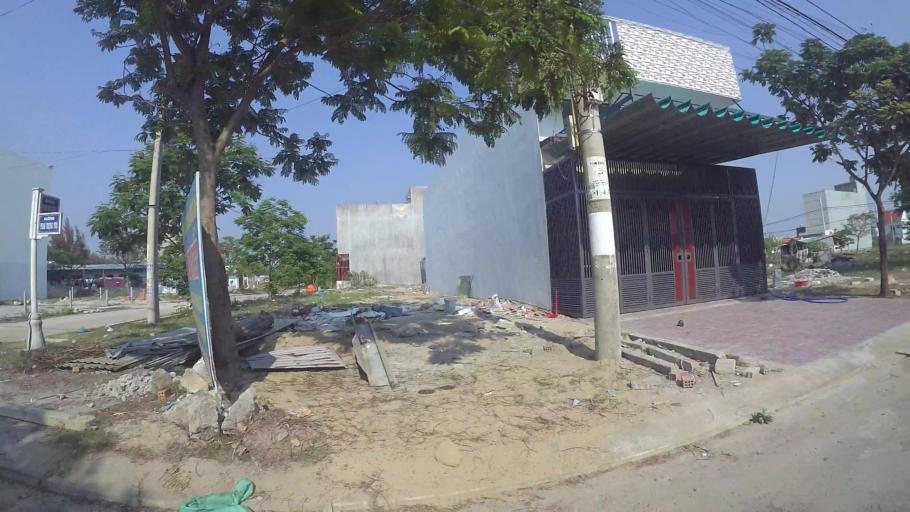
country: VN
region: Da Nang
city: Ngu Hanh Son
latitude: 15.9534
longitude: 108.2595
